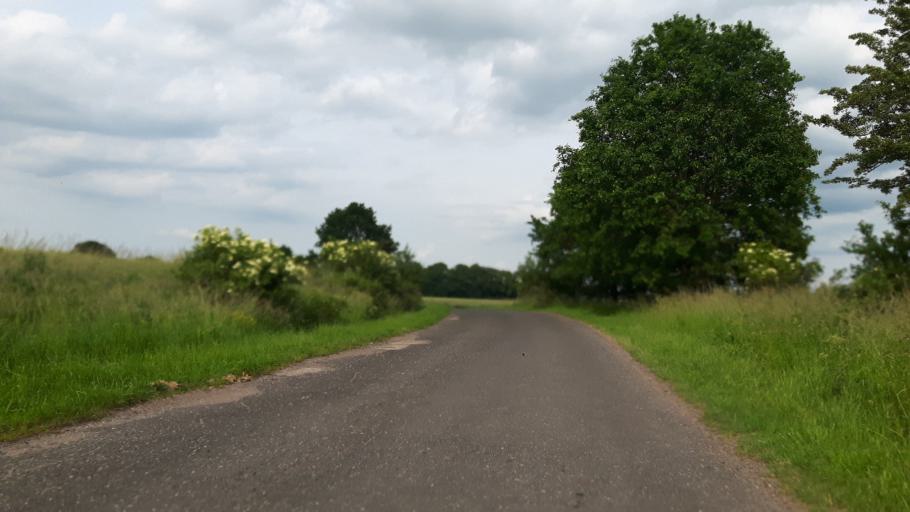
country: PL
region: West Pomeranian Voivodeship
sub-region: Powiat gryficki
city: Gryfice
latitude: 53.8344
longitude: 15.1498
